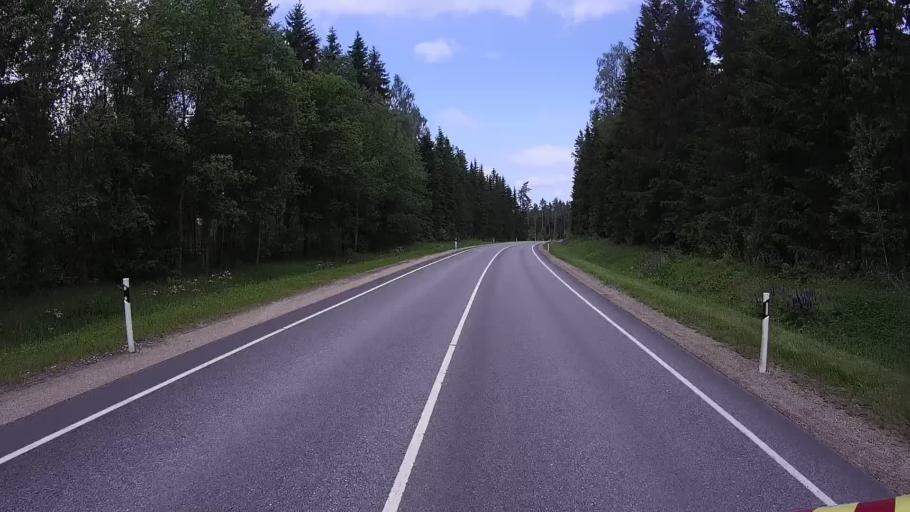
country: EE
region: Polvamaa
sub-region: Polva linn
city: Polva
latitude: 58.1177
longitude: 26.9588
